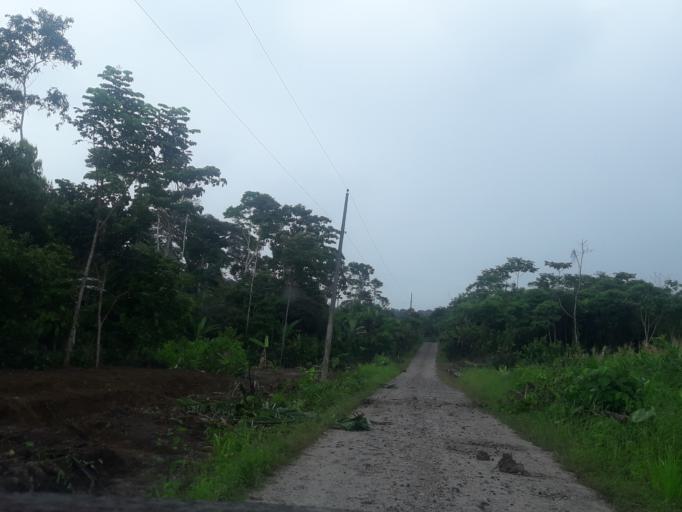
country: EC
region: Napo
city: Tena
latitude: -1.1013
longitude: -77.6854
